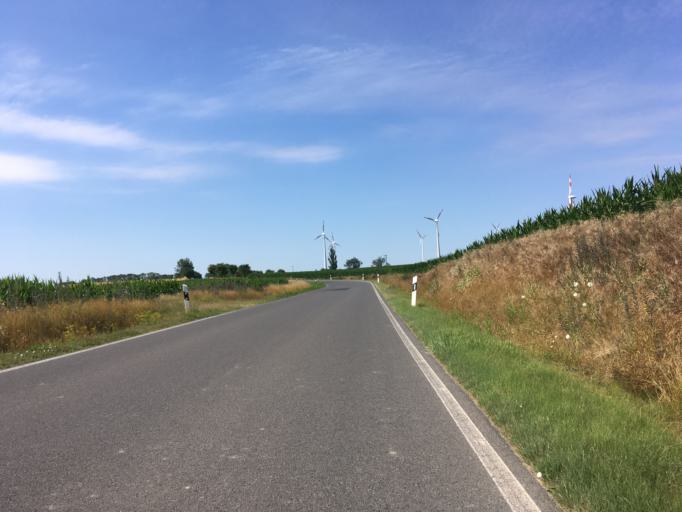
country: DE
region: Brandenburg
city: Gramzow
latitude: 53.2663
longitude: 14.0681
